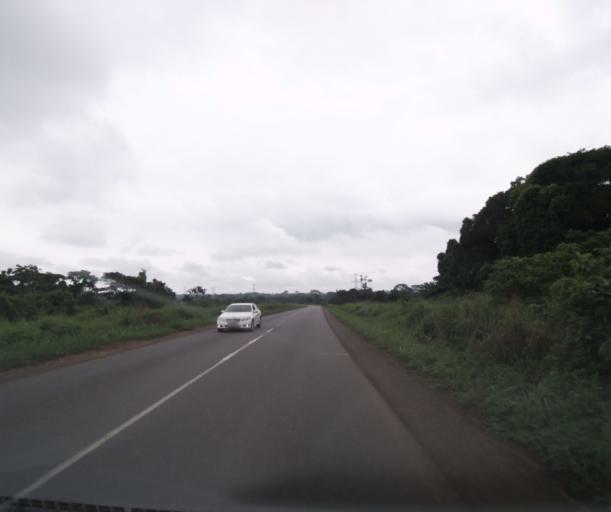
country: CM
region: Littoral
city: Edea
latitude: 3.7493
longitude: 10.1208
